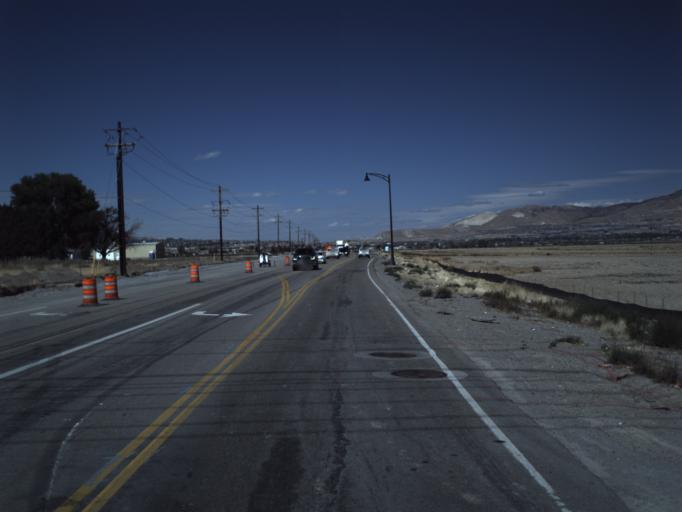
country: US
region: Utah
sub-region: Utah County
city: Saratoga Springs
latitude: 40.3550
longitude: -111.9162
